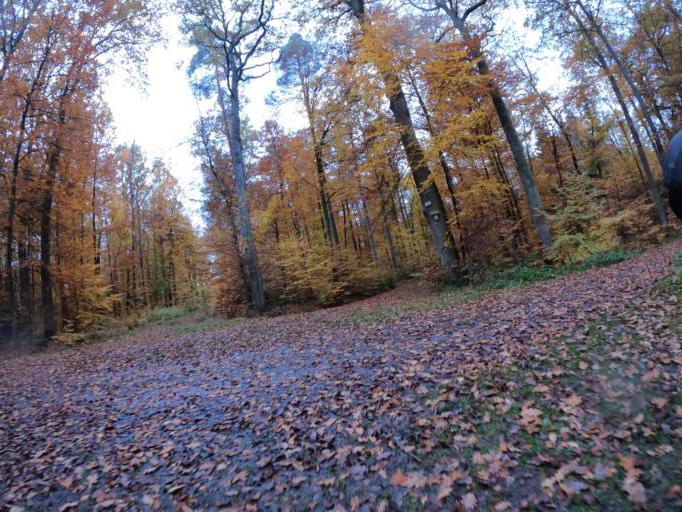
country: DE
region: Baden-Wuerttemberg
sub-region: Regierungsbezirk Stuttgart
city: Hildrizhausen
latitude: 48.6097
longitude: 8.9624
